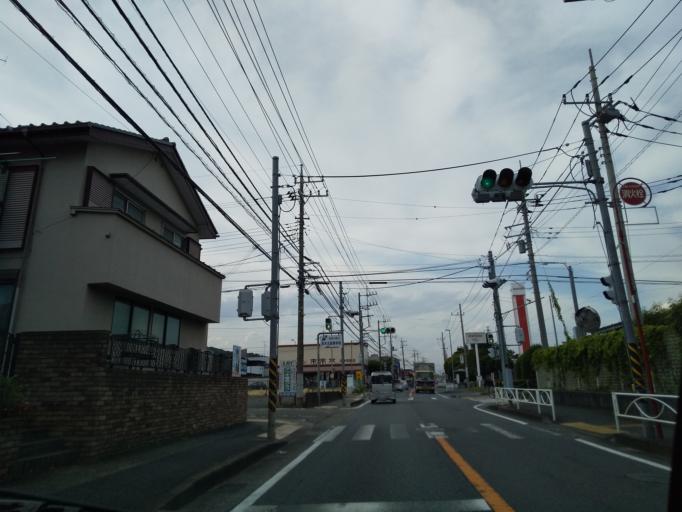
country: JP
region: Kanagawa
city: Zama
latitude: 35.4875
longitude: 139.3404
